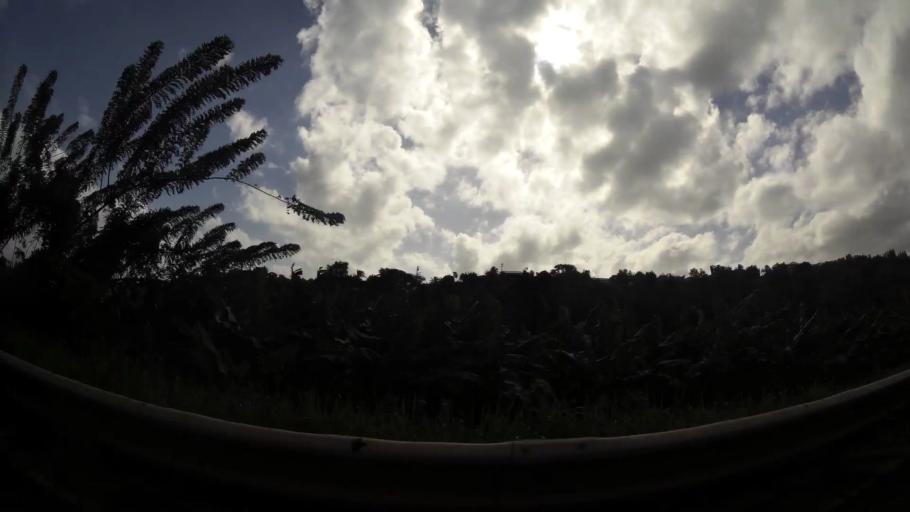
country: MQ
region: Martinique
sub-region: Martinique
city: Le Francois
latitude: 14.6092
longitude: -60.8869
